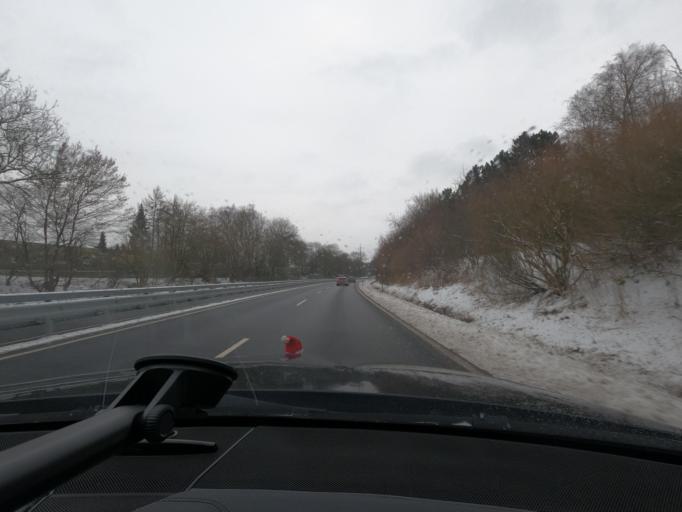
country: DE
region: Schleswig-Holstein
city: Harrislee
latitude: 54.8037
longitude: 9.4055
